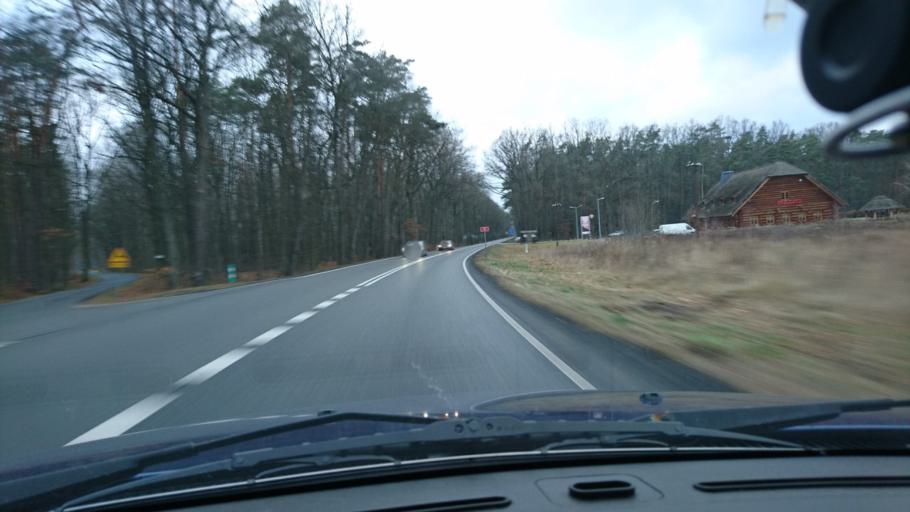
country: PL
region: Opole Voivodeship
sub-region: Powiat oleski
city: Olesno
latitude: 50.9211
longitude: 18.3393
